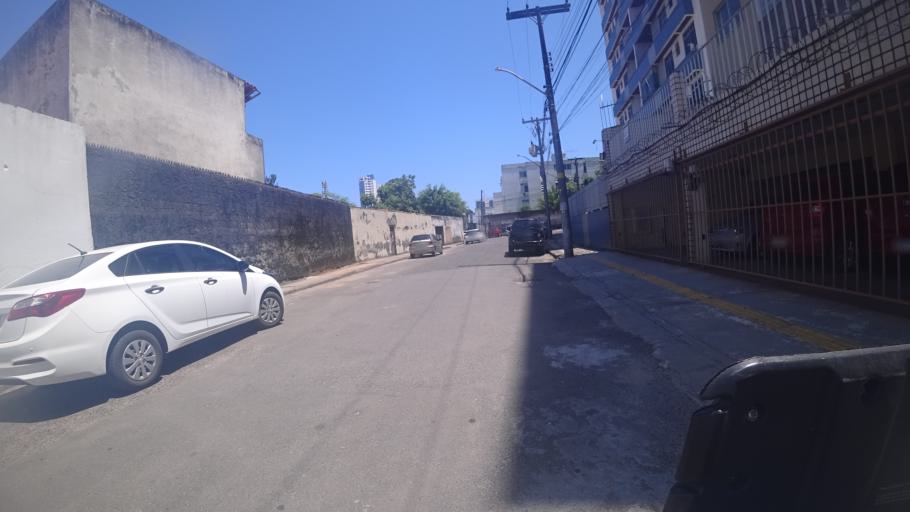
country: BR
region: Bahia
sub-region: Salvador
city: Salvador
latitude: -12.9880
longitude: -38.4579
